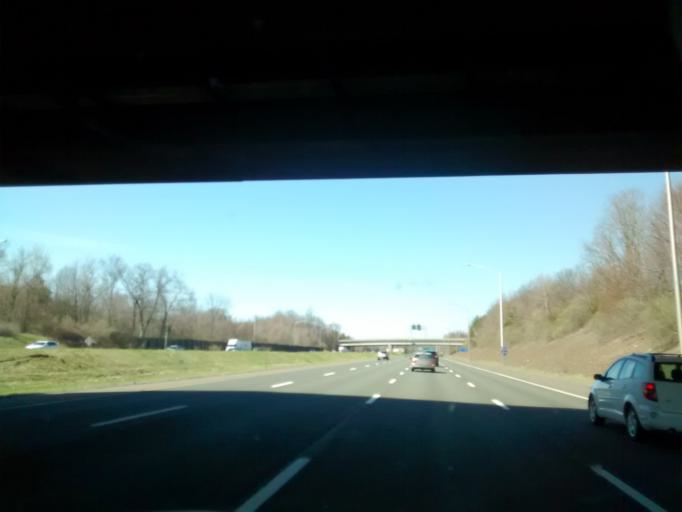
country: US
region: Connecticut
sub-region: Tolland County
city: Rockville
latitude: 41.8262
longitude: -72.4887
